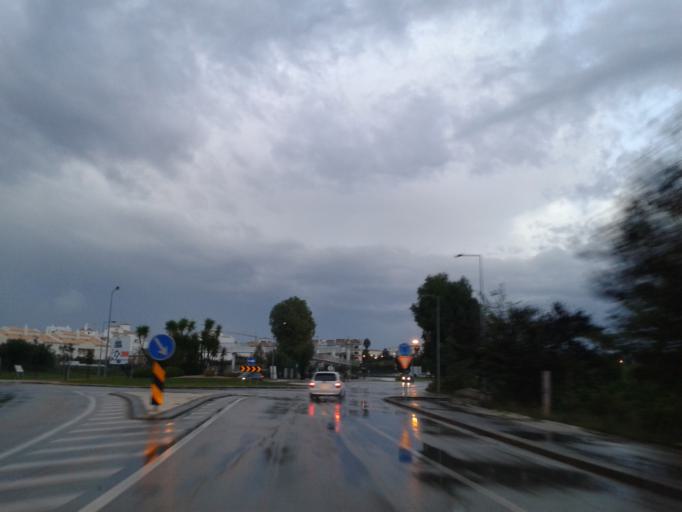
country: PT
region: Faro
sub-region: Lagoa
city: Lagoa
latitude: 37.1362
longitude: -8.4639
